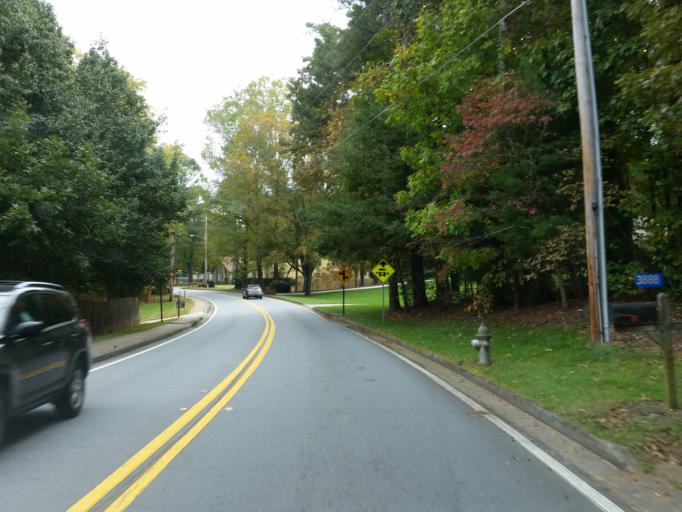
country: US
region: Georgia
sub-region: Fulton County
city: Sandy Springs
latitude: 33.9841
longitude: -84.4387
